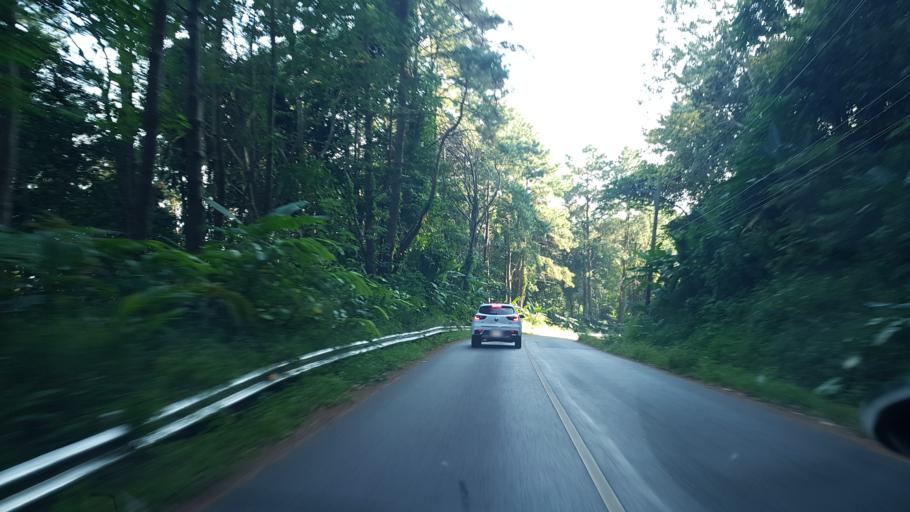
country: TH
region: Chiang Rai
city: Mae Fa Luang
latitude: 20.3246
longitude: 99.8245
